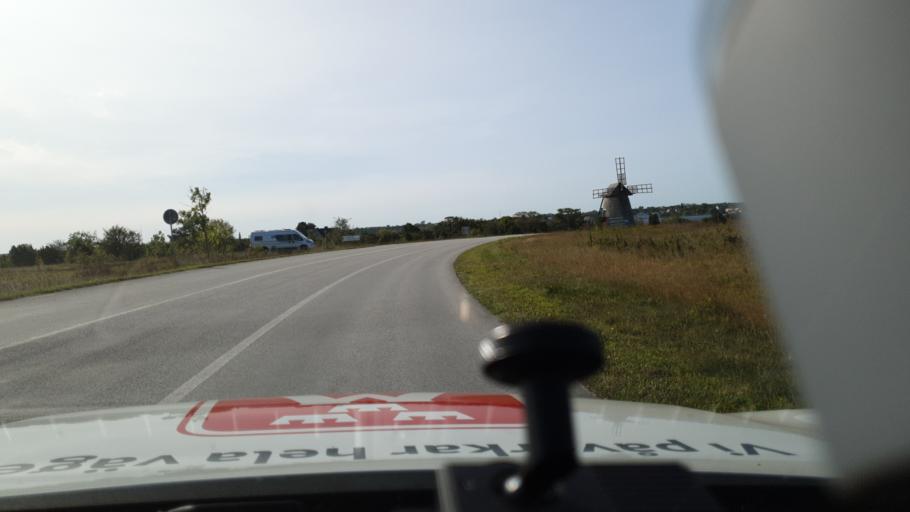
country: SE
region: Gotland
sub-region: Gotland
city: Slite
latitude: 57.8702
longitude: 19.0855
